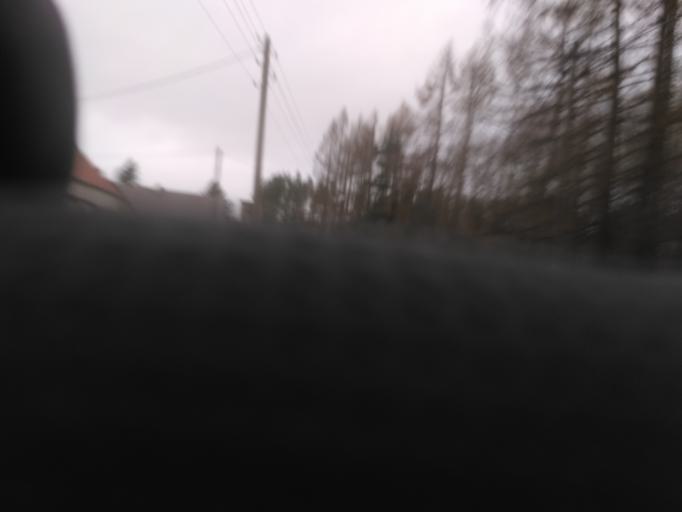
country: DE
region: Saxony
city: Weinbohla
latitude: 51.1726
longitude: 13.6163
